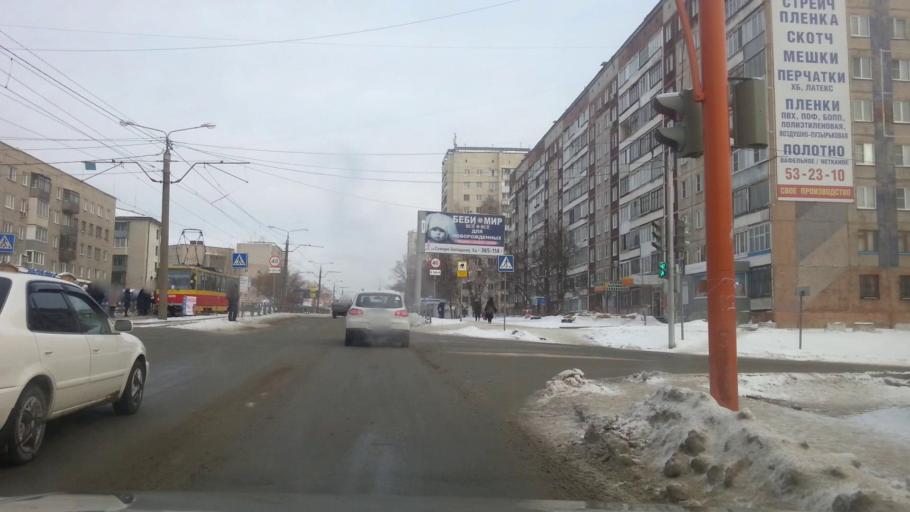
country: RU
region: Altai Krai
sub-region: Gorod Barnaulskiy
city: Barnaul
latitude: 53.3701
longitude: 83.7419
